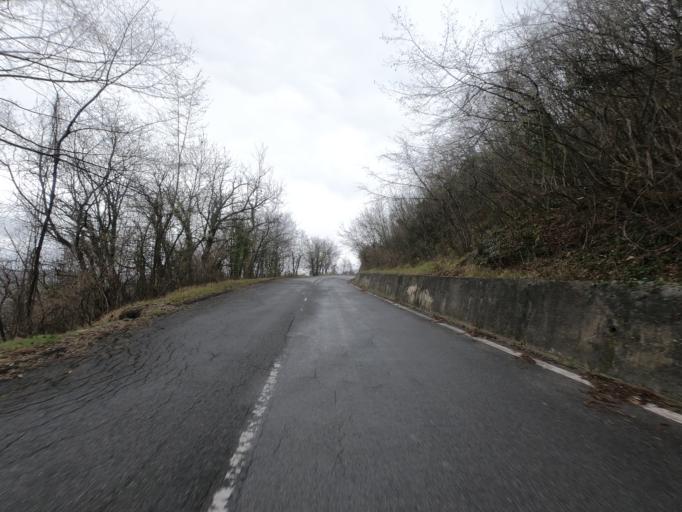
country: IT
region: Liguria
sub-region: Provincia di Imperia
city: Cesio
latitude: 44.0239
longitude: 7.9925
